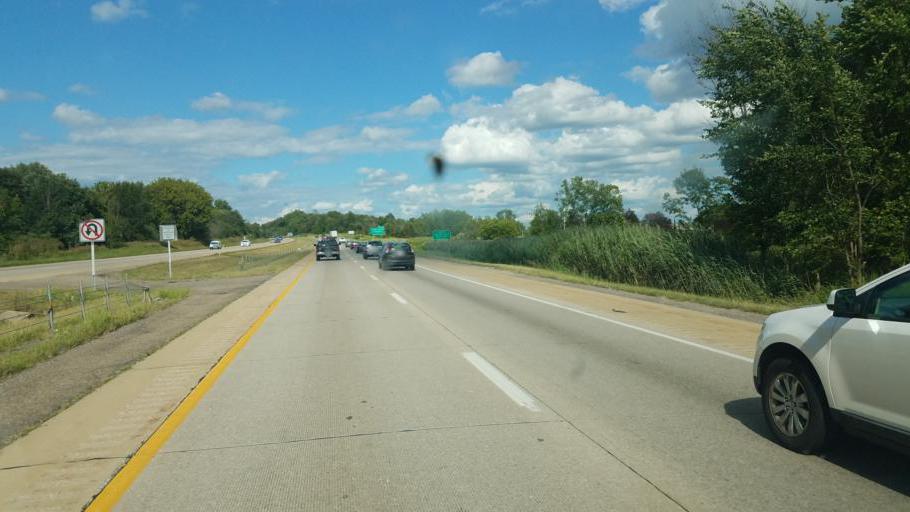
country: US
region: Ohio
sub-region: Summit County
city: Mogadore
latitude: 41.0865
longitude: -81.3914
